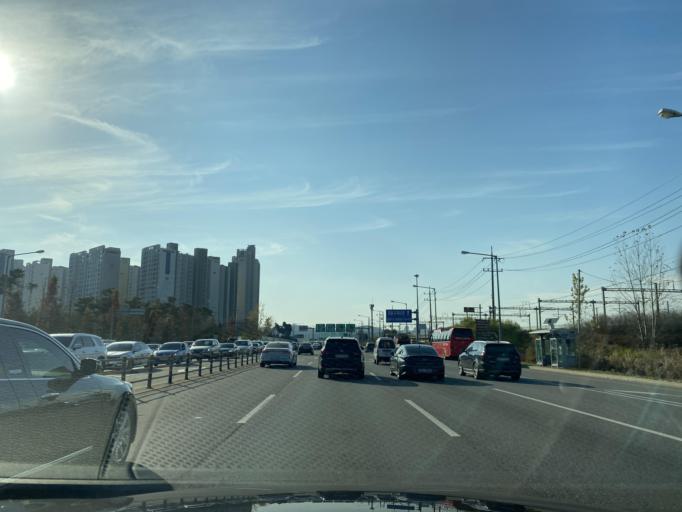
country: KR
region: Chungcheongnam-do
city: Asan
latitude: 36.7767
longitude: 127.0532
